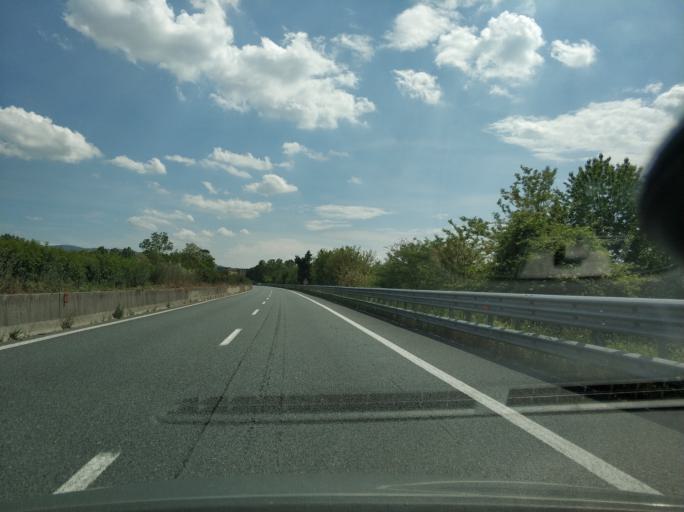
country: IT
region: Piedmont
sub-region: Provincia di Torino
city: Turin
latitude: 45.1197
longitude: 7.6947
